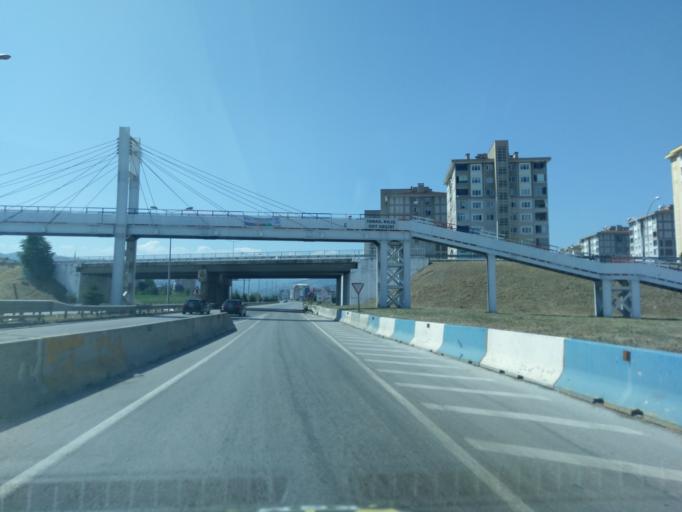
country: TR
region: Samsun
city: Samsun
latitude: 41.2642
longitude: 36.3476
